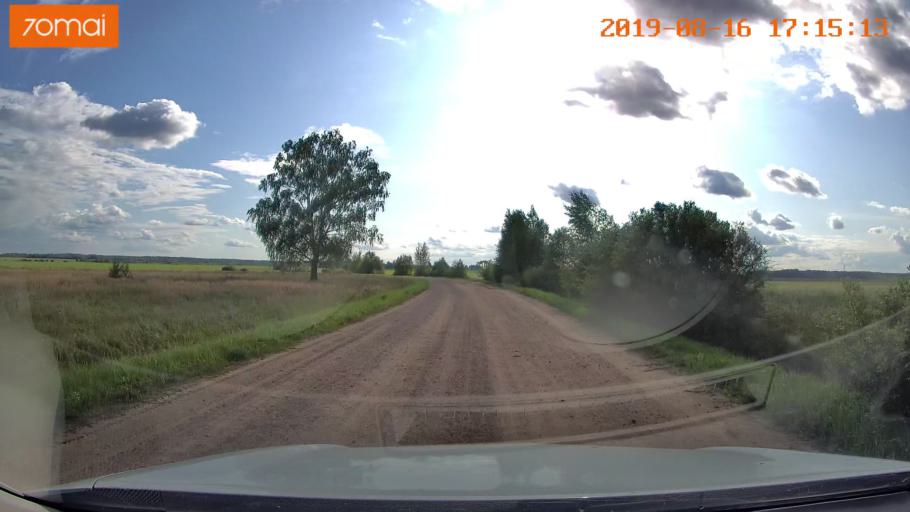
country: BY
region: Mogilev
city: Hlusha
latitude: 53.1803
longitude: 28.8464
